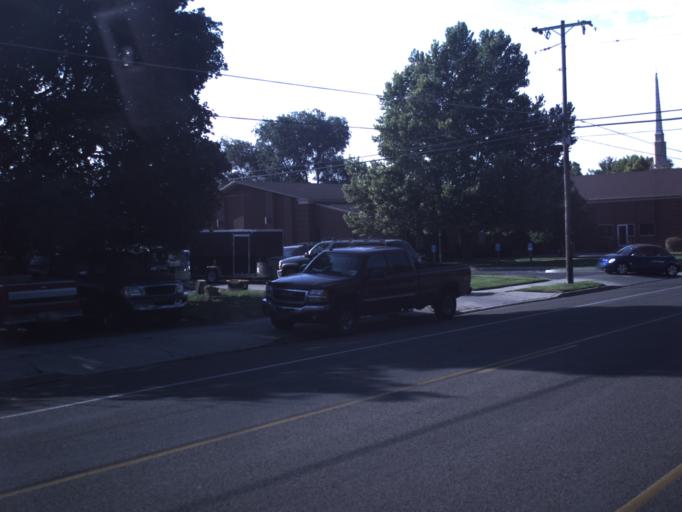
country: US
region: Utah
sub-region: Utah County
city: American Fork
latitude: 40.3844
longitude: -111.7959
